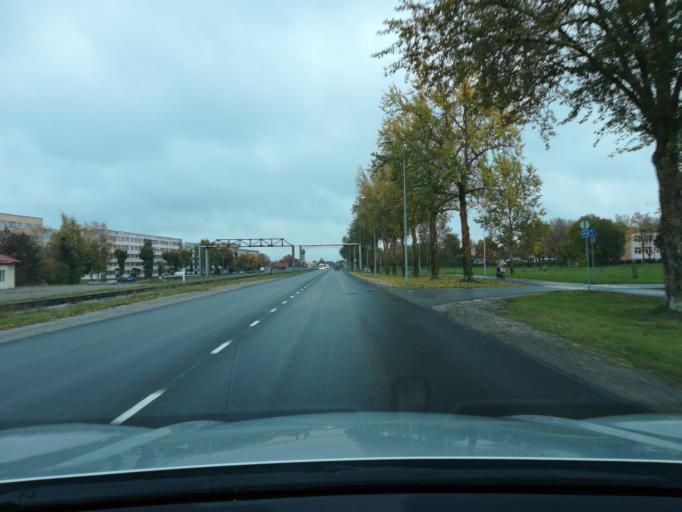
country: EE
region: Ida-Virumaa
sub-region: Johvi vald
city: Johvi
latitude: 59.3313
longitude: 27.4117
